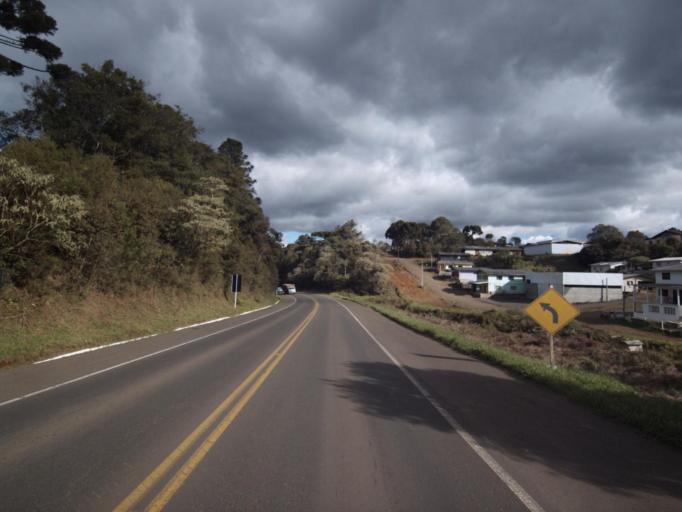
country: BR
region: Santa Catarina
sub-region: Joacaba
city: Joacaba
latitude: -27.0735
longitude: -51.6630
